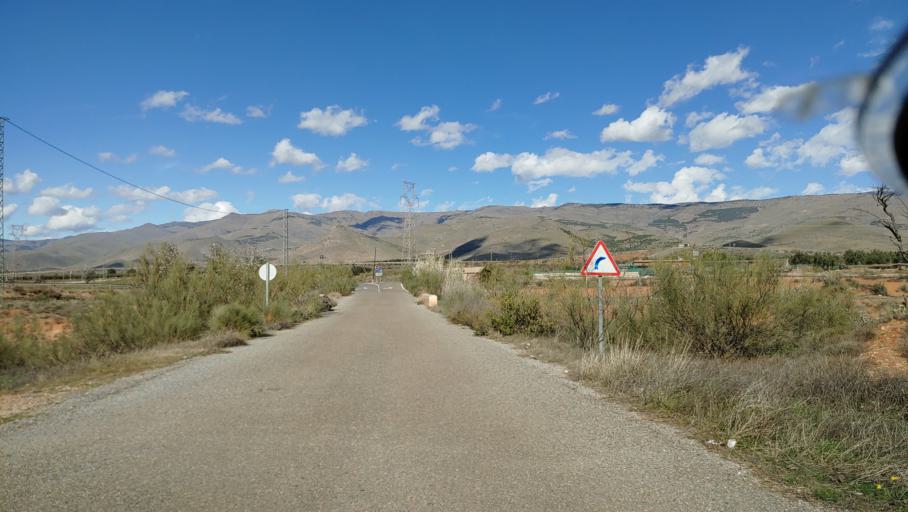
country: ES
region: Andalusia
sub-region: Provincia de Almeria
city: Gergal
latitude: 37.1108
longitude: -2.5920
